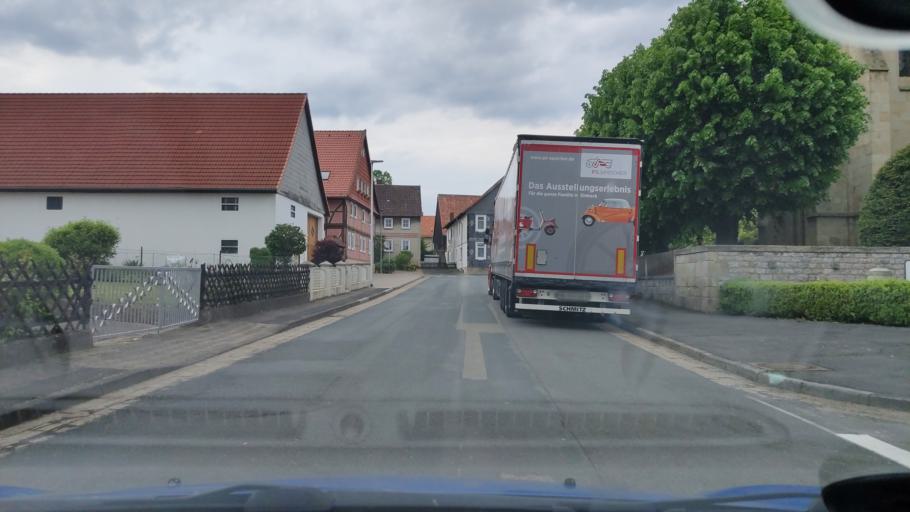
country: DE
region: Lower Saxony
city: Freden
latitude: 51.8892
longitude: 9.8603
